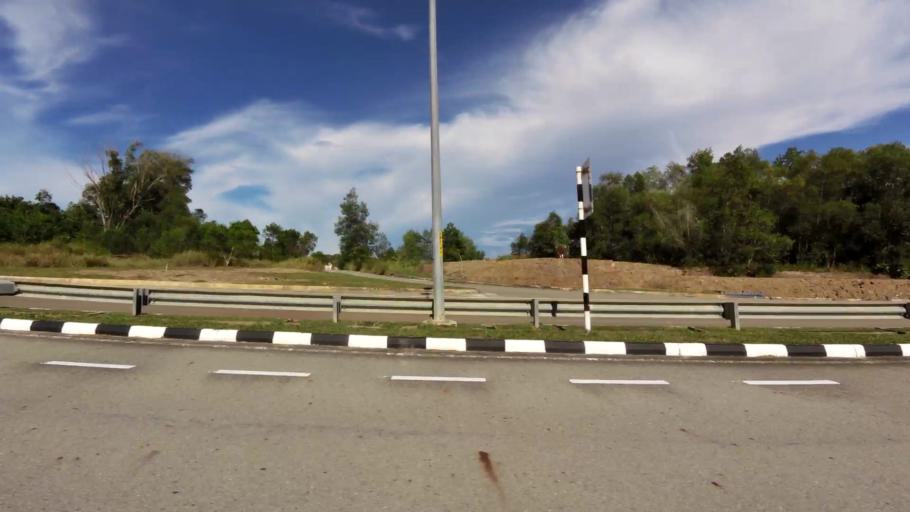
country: BN
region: Brunei and Muara
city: Bandar Seri Begawan
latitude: 4.9788
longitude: 114.9330
